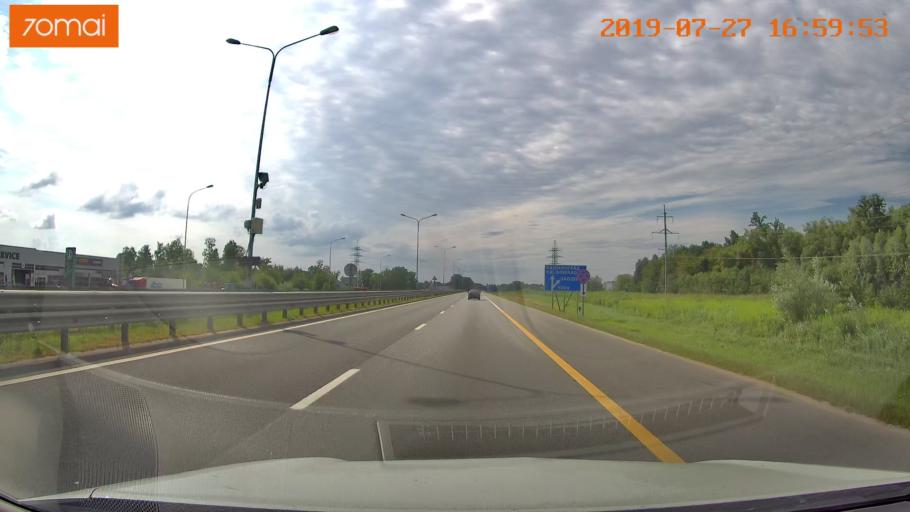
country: RU
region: Kaliningrad
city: Bol'shoe Isakovo
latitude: 54.7059
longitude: 20.6378
